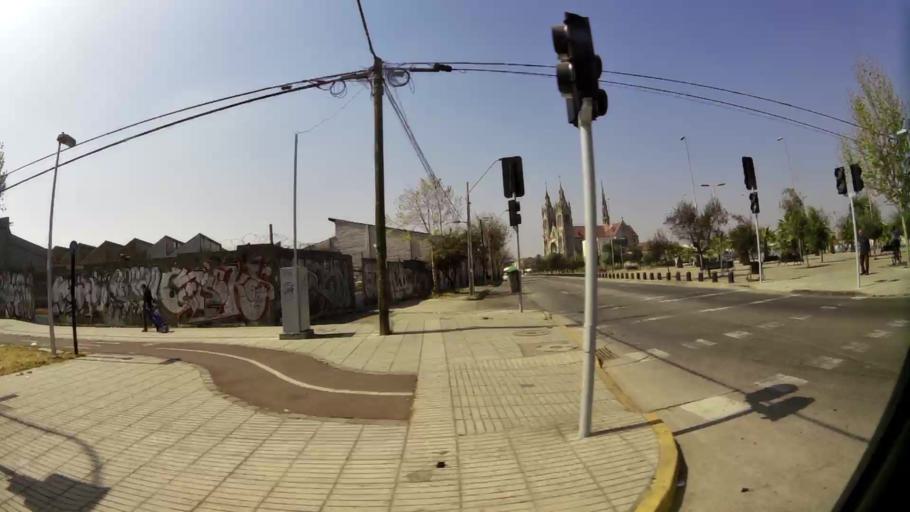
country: CL
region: Santiago Metropolitan
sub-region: Provincia de Santiago
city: Santiago
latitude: -33.4583
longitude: -70.6783
